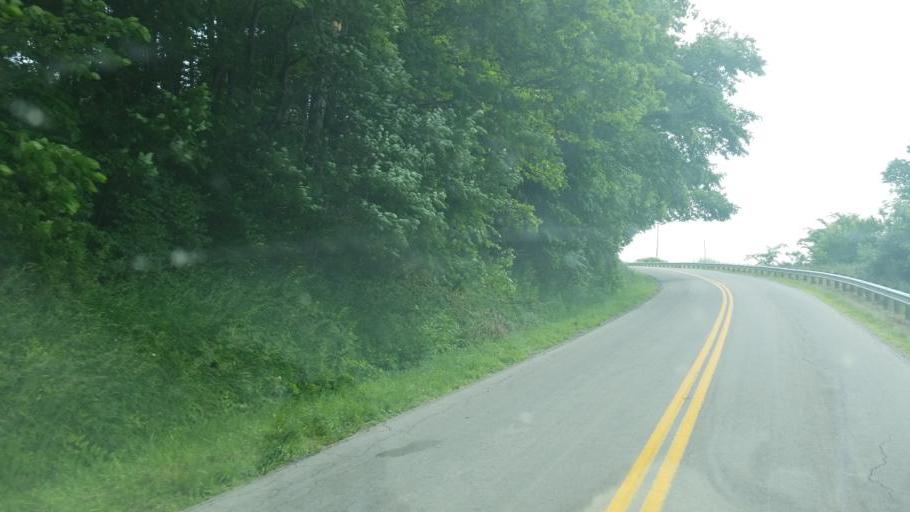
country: US
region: Ohio
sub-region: Ashland County
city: Loudonville
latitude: 40.6807
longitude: -82.2283
